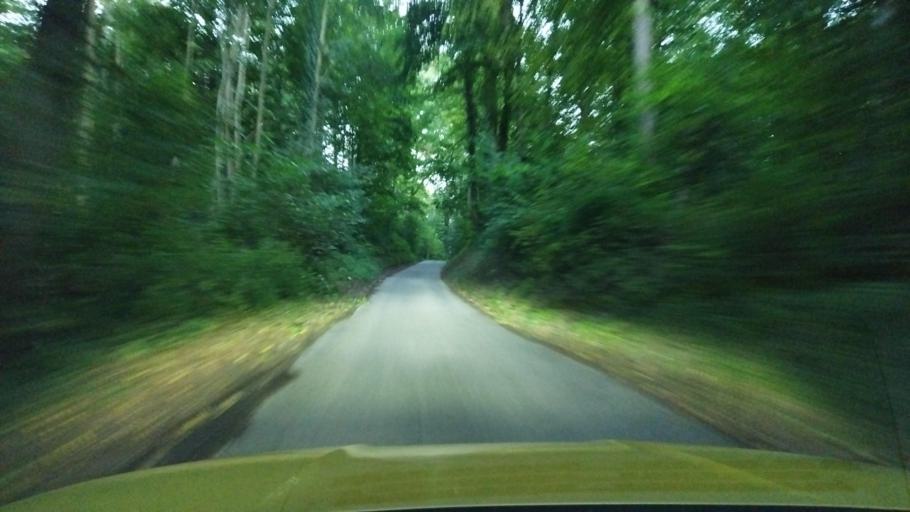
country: DE
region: Baden-Wuerttemberg
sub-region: Regierungsbezirk Stuttgart
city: Bad Wimpfen
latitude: 49.2104
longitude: 9.1695
